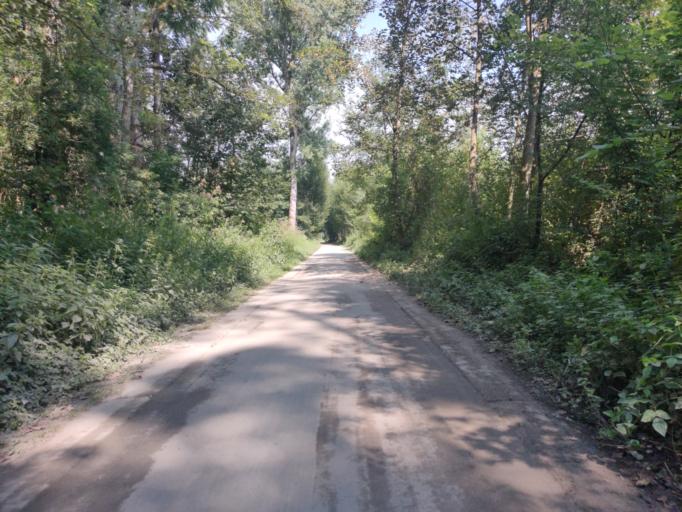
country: AT
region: Lower Austria
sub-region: Politischer Bezirk Amstetten
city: Zeillern
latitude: 48.1863
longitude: 14.7956
